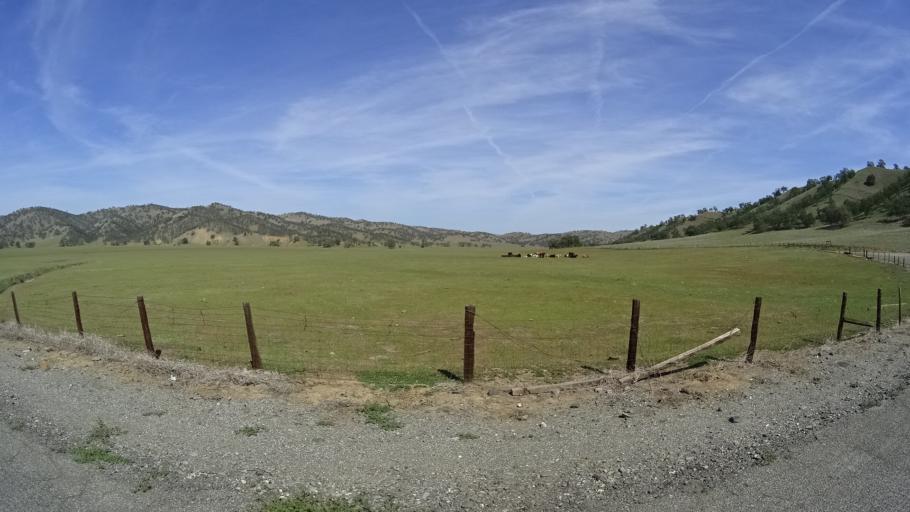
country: US
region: California
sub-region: Glenn County
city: Willows
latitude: 39.5383
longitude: -122.4398
